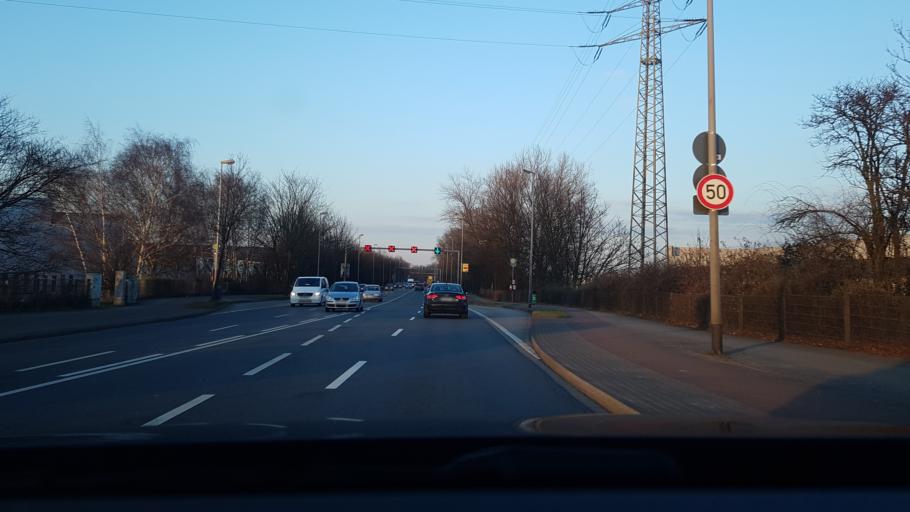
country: DE
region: North Rhine-Westphalia
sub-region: Regierungsbezirk Dusseldorf
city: Hochfeld
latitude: 51.4161
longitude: 6.7409
